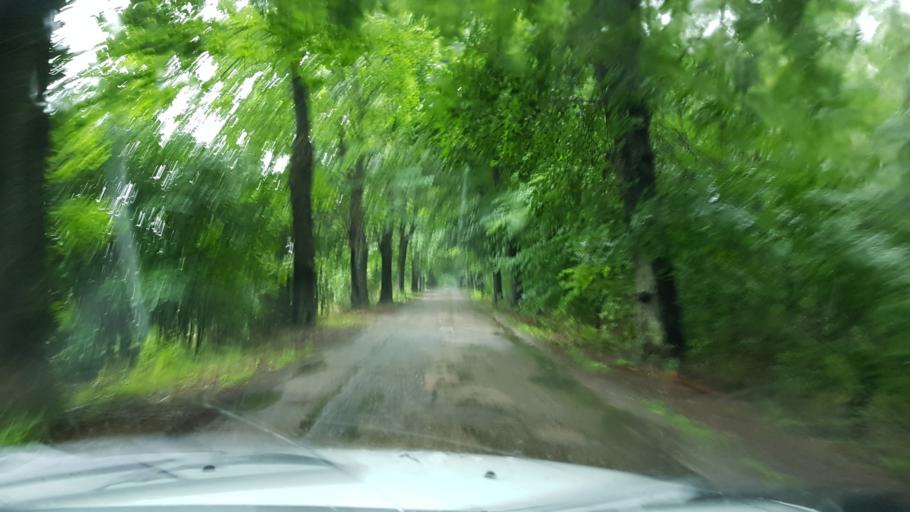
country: PL
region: West Pomeranian Voivodeship
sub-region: Powiat kolobrzeski
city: Ryman
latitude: 53.9588
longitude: 15.4452
